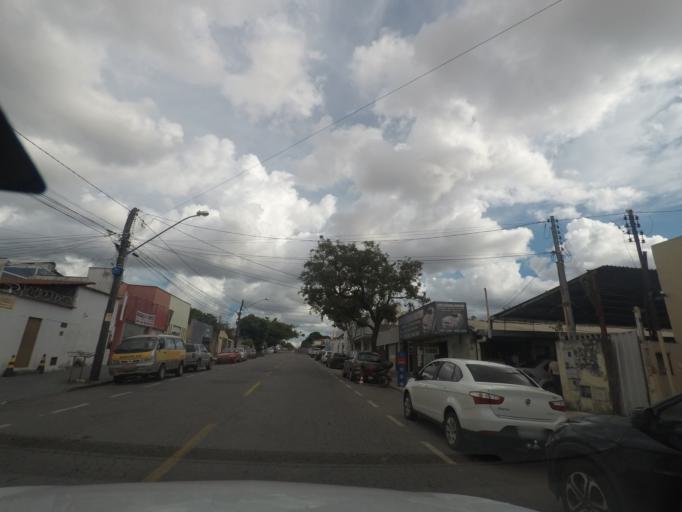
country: BR
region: Goias
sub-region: Goiania
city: Goiania
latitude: -16.7145
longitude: -49.2829
